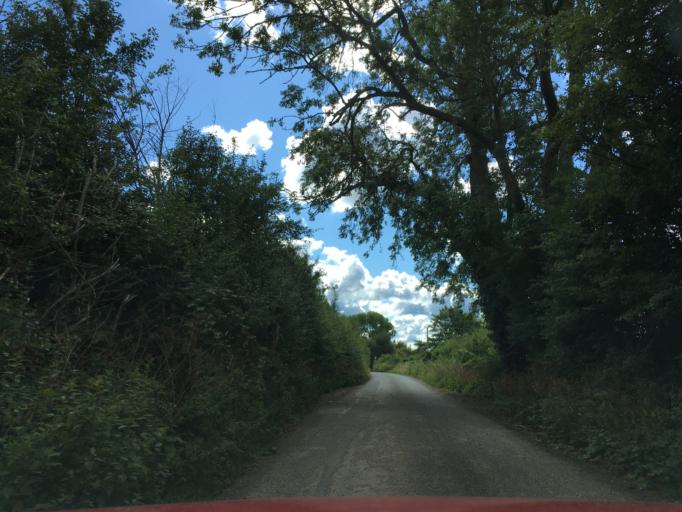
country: GB
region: England
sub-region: Gloucestershire
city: Newent
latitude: 51.8493
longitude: -2.3502
